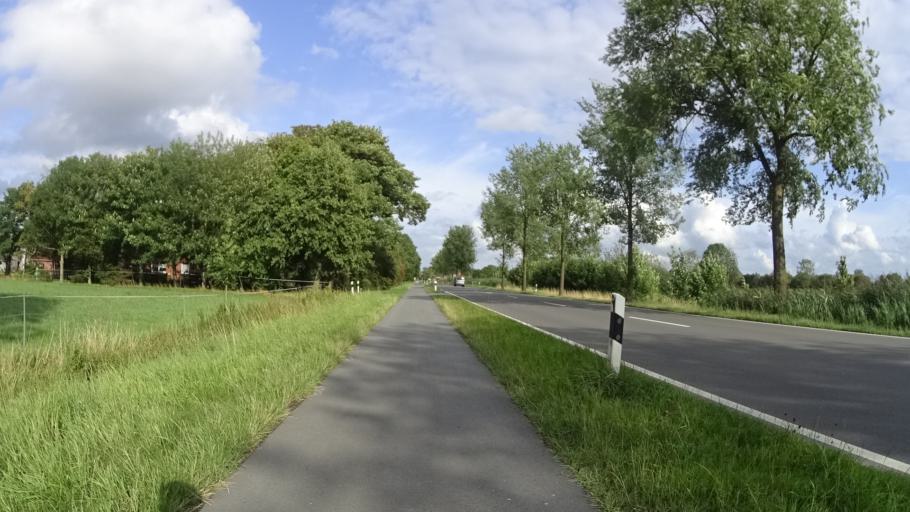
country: DE
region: Lower Saxony
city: Varel
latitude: 53.3861
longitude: 8.2240
